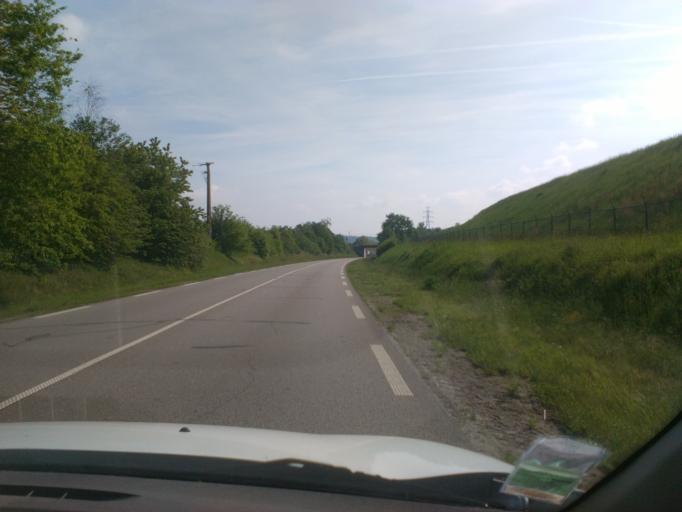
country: FR
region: Lorraine
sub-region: Departement des Vosges
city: Chavelot
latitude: 48.2171
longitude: 6.4242
